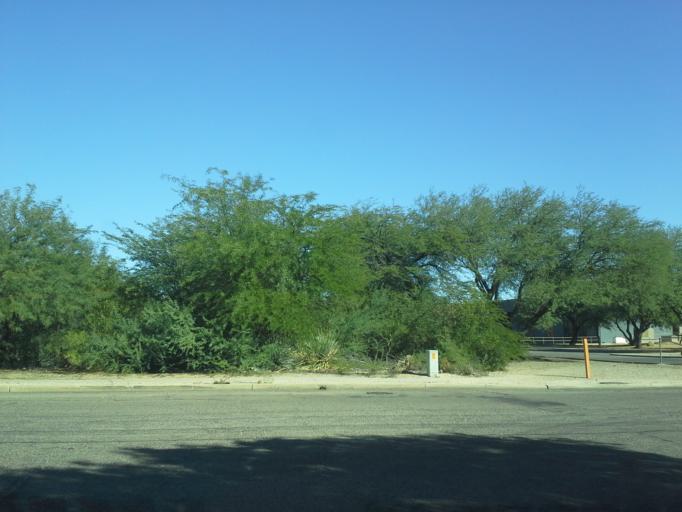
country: US
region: Arizona
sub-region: Pima County
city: Summit
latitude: 32.1267
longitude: -110.9327
